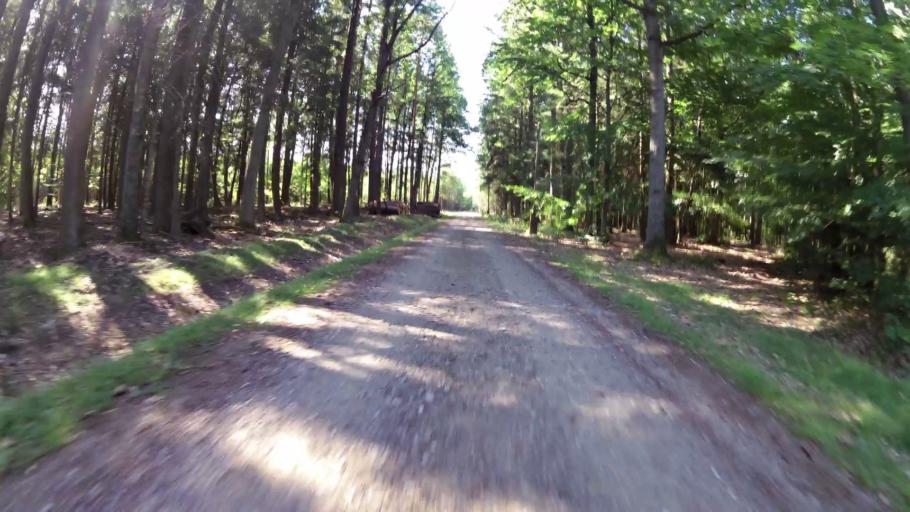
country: PL
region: West Pomeranian Voivodeship
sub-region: Powiat drawski
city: Czaplinek
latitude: 53.4013
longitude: 16.2466
